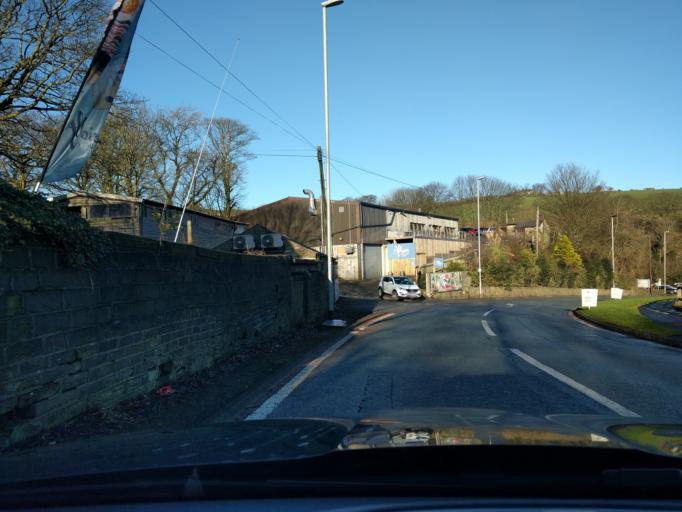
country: GB
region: England
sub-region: Borough of Oldham
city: Delph
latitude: 53.5581
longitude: -2.0329
